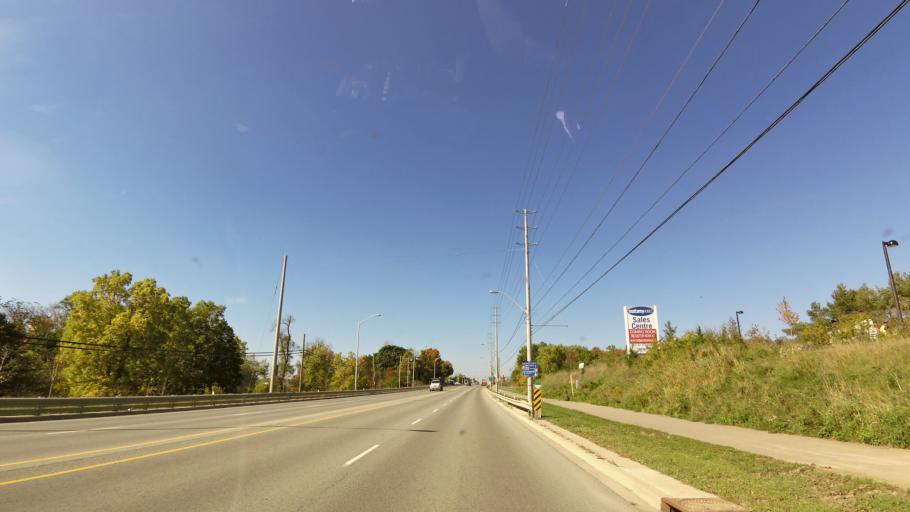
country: CA
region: Ontario
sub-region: Halton
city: Milton
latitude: 43.5039
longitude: -79.8578
